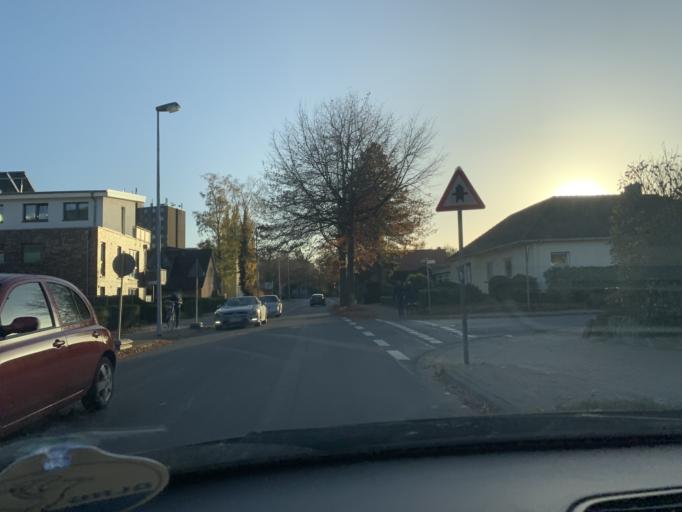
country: DE
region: Lower Saxony
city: Oldenburg
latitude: 53.1424
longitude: 8.1764
